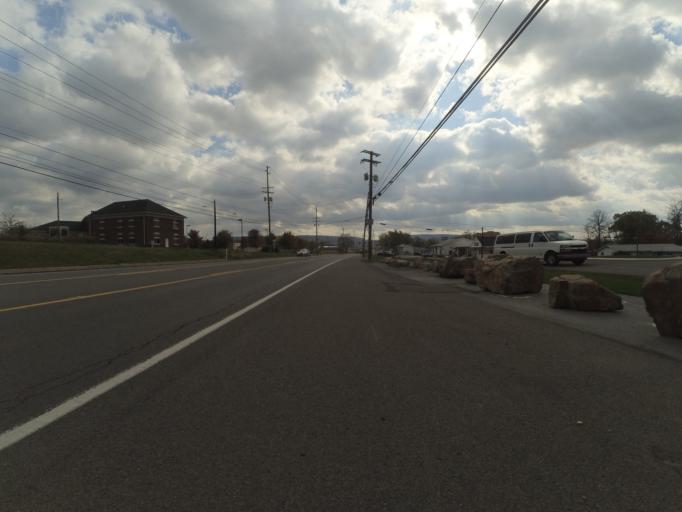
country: US
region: Pennsylvania
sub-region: Centre County
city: Bellefonte
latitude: 40.8890
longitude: -77.7825
